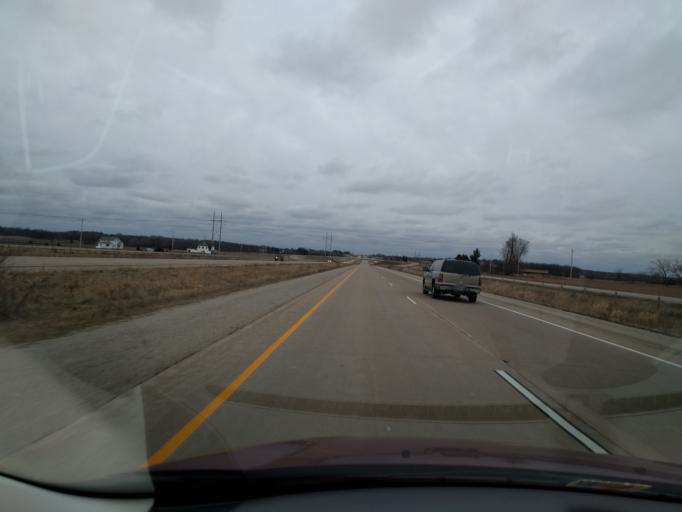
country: US
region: Wisconsin
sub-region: Winnebago County
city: Winneconne
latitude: 44.1757
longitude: -88.6645
